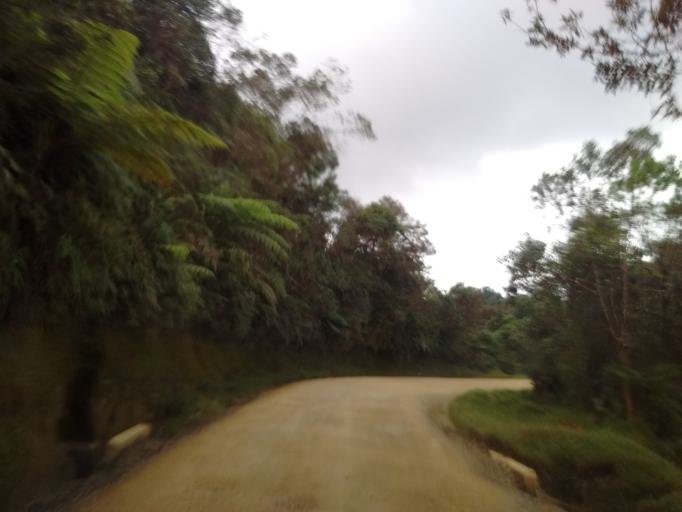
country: CO
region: Huila
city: Isnos
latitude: 2.0258
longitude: -76.2720
